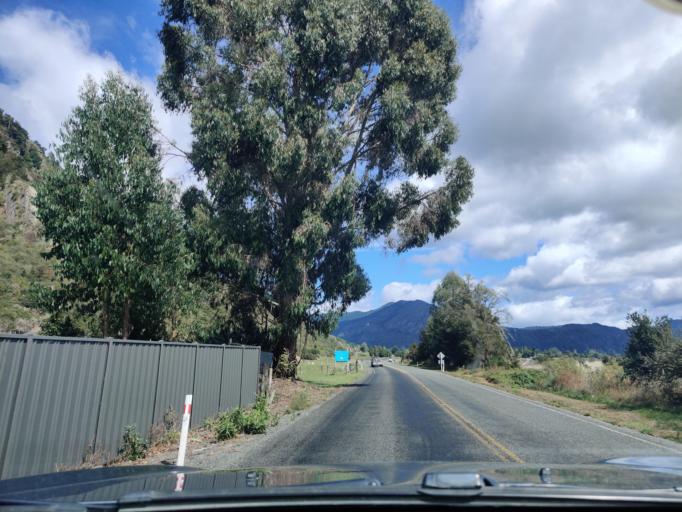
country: NZ
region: West Coast
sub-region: Buller District
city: Westport
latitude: -41.7958
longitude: 172.3638
